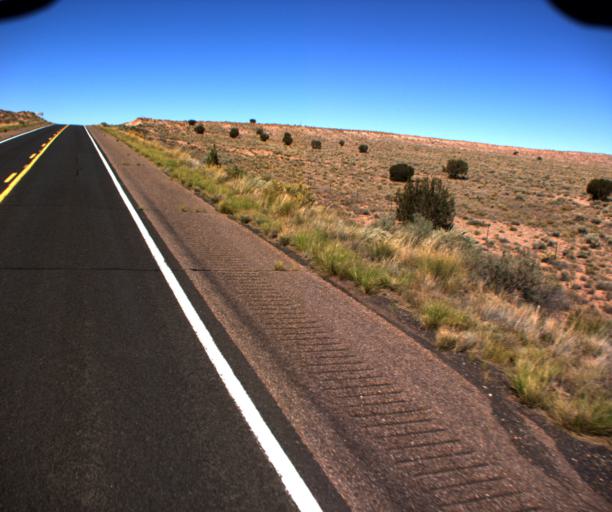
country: US
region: Arizona
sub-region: Navajo County
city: Snowflake
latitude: 34.6857
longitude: -109.7391
